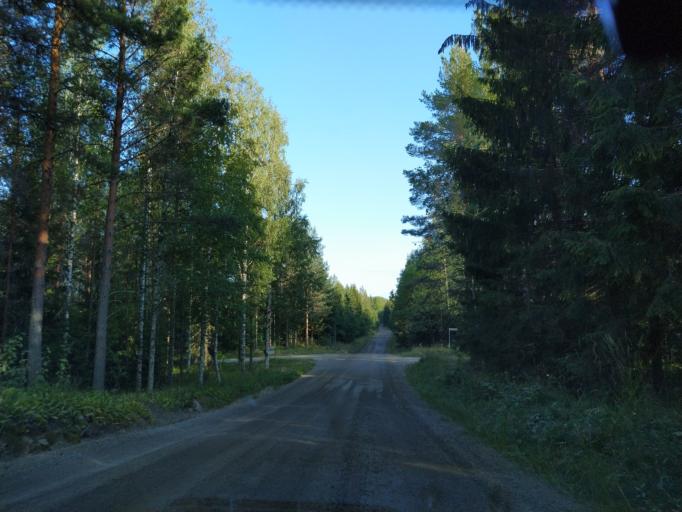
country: FI
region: Central Finland
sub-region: Jaemsae
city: Kuhmoinen
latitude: 61.6091
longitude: 25.1271
